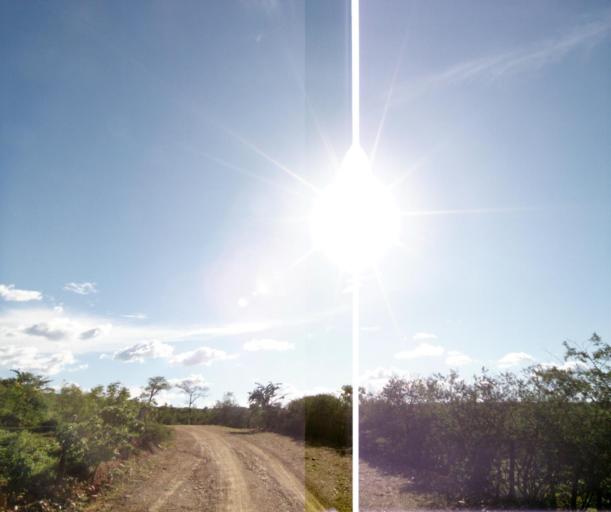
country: BR
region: Bahia
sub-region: Tanhacu
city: Tanhacu
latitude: -14.1842
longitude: -40.9346
